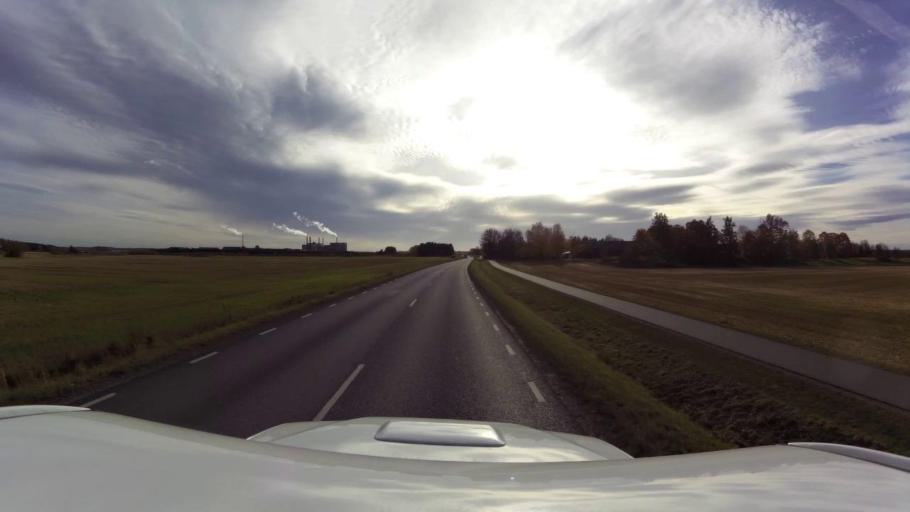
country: SE
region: OEstergoetland
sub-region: Linkopings Kommun
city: Ekangen
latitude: 58.4481
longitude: 15.6452
